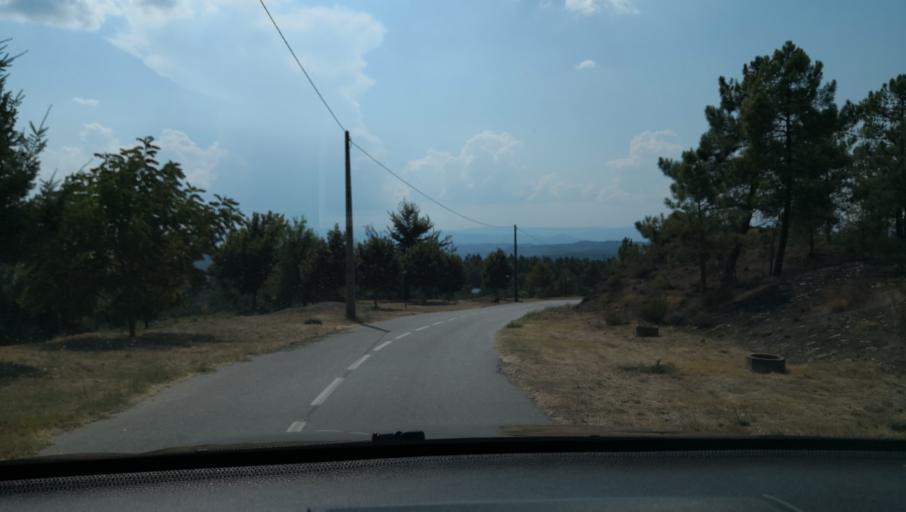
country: PT
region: Vila Real
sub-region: Sabrosa
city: Sabrosa
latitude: 41.2773
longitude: -7.6182
